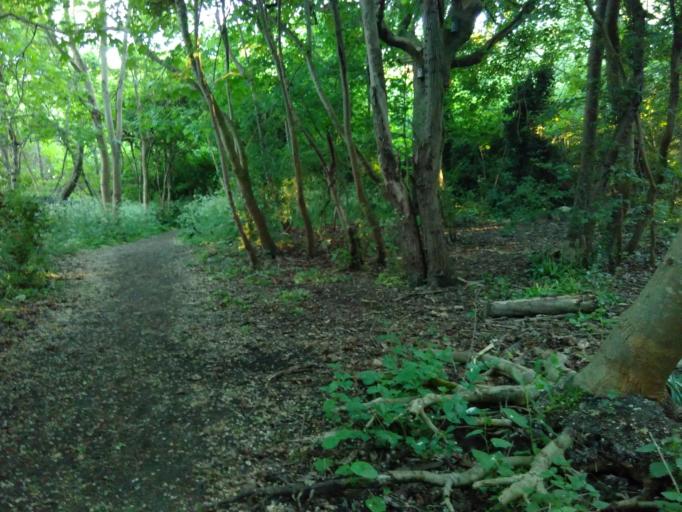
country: GB
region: England
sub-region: Greater London
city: Hammersmith
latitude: 51.4851
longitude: -0.2456
